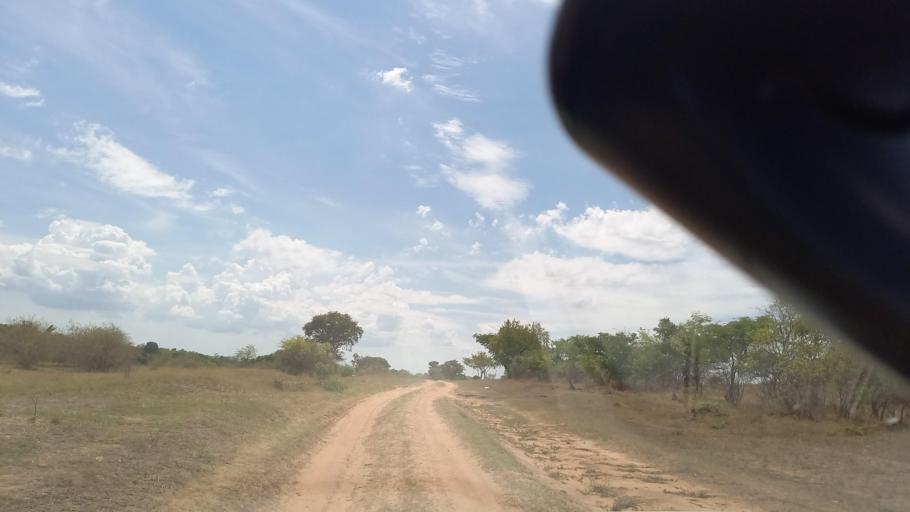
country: ZM
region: Southern
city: Mazabuka
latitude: -16.1397
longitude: 27.7618
